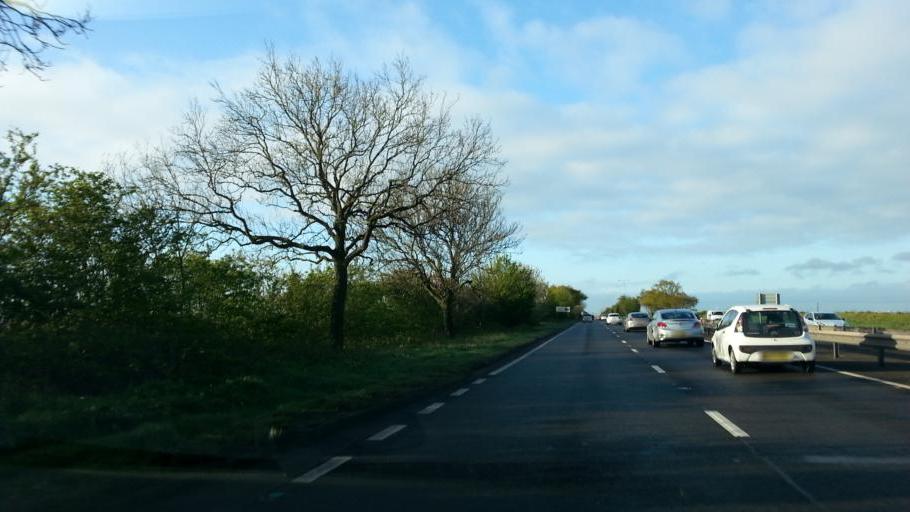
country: GB
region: England
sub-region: Leicestershire
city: Queniborough
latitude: 52.7533
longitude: -1.0598
